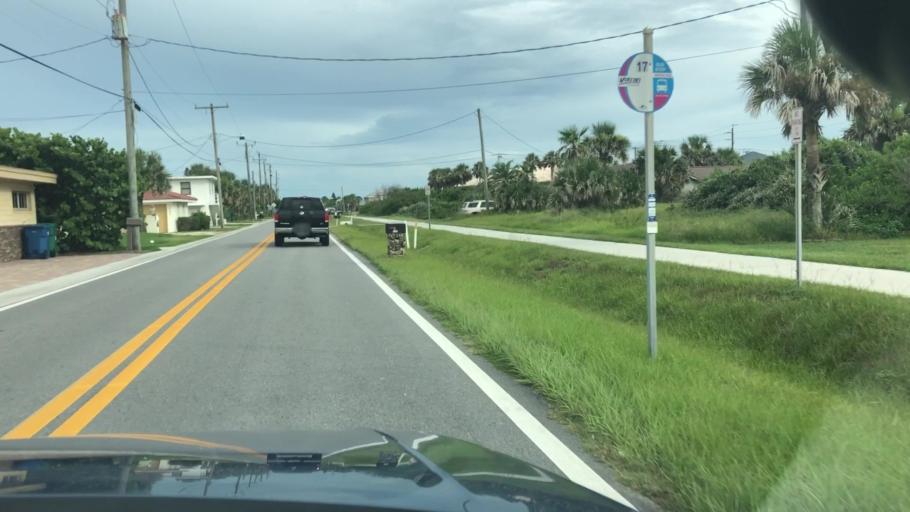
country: US
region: Florida
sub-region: Volusia County
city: Ponce Inlet
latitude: 29.1245
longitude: -80.9538
